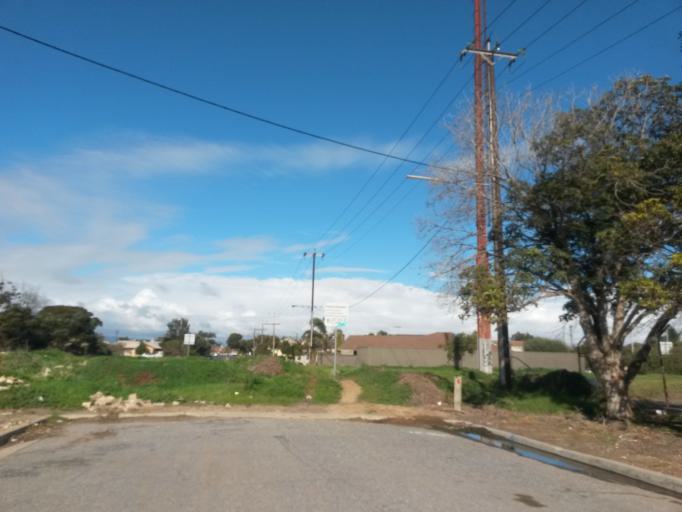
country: AU
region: South Australia
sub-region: Port Adelaide Enfield
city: Alberton
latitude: -34.8463
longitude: 138.5207
